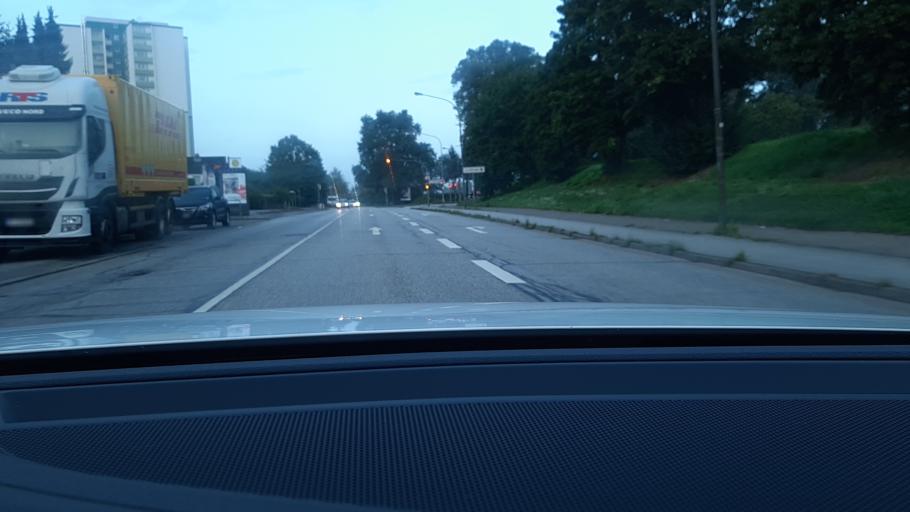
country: DE
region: Schleswig-Holstein
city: Stockelsdorf
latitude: 53.8529
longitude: 10.6349
